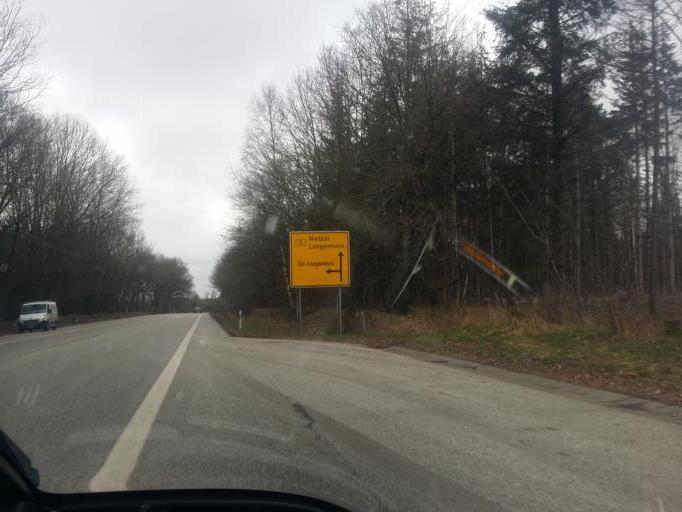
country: DE
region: Schleswig-Holstein
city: Bordelum
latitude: 54.6574
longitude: 8.9494
